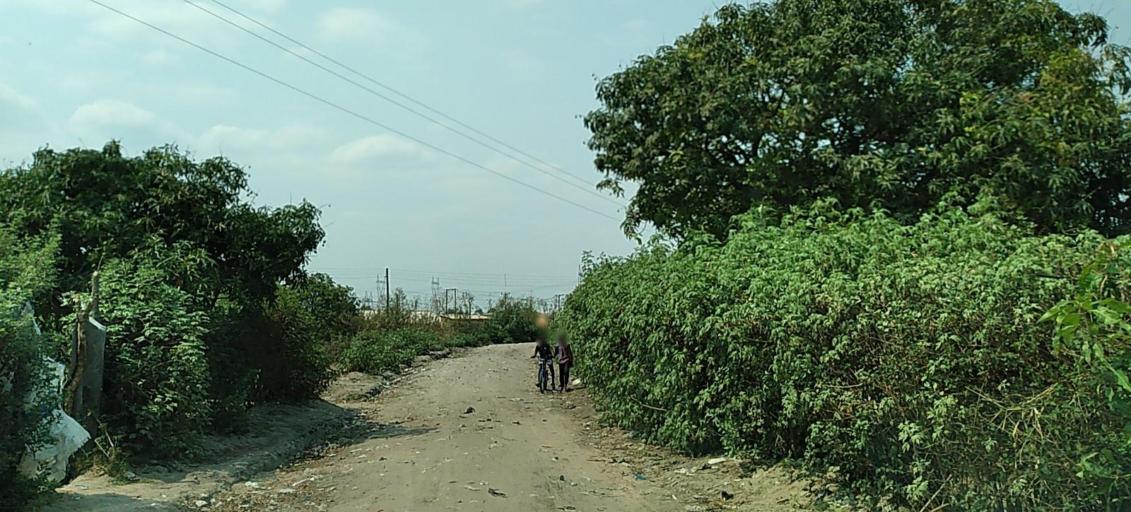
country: ZM
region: Copperbelt
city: Chambishi
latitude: -12.6305
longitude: 28.0745
